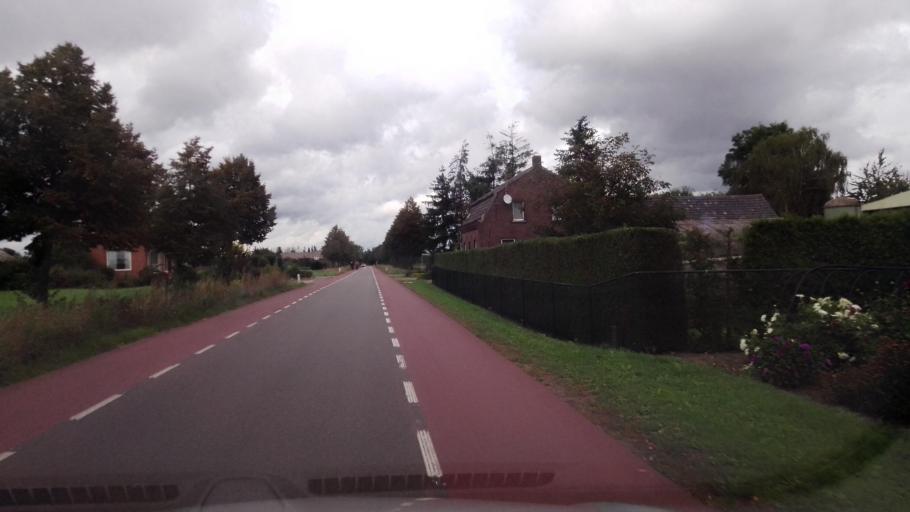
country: NL
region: Limburg
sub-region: Gemeente Peel en Maas
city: Maasbree
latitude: 51.3778
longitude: 6.0510
